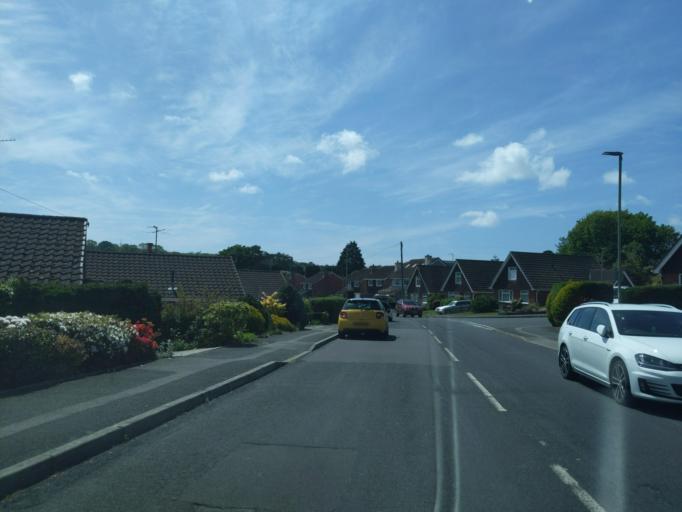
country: GB
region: England
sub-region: Devon
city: Ivybridge
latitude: 50.3895
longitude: -3.9307
